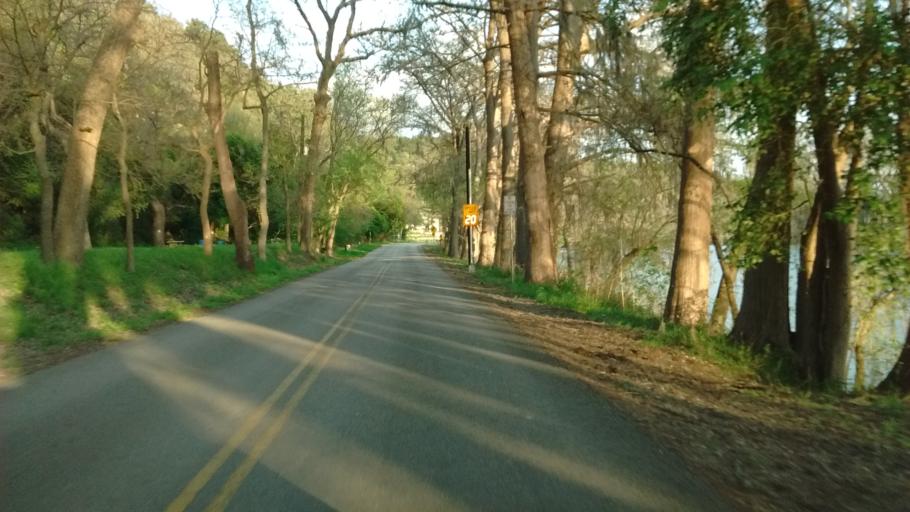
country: US
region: Texas
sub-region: Comal County
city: New Braunfels
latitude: 29.7665
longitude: -98.1436
